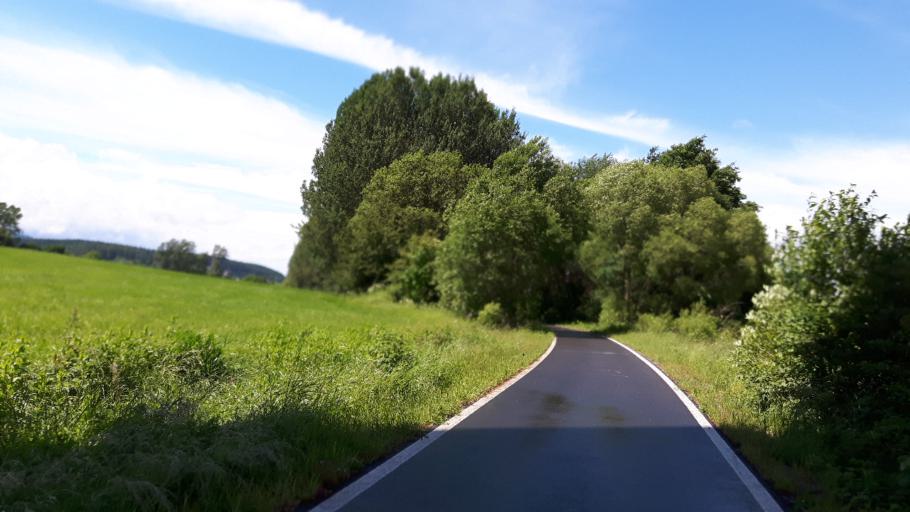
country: DE
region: Thuringia
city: Langewiesen
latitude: 50.6637
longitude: 10.9862
